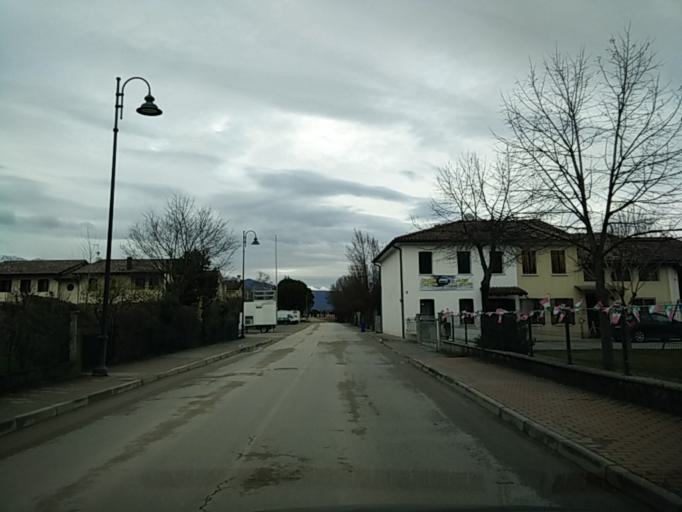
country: IT
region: Veneto
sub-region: Provincia di Treviso
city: Loria Bessica
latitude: 45.7514
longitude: 11.8791
